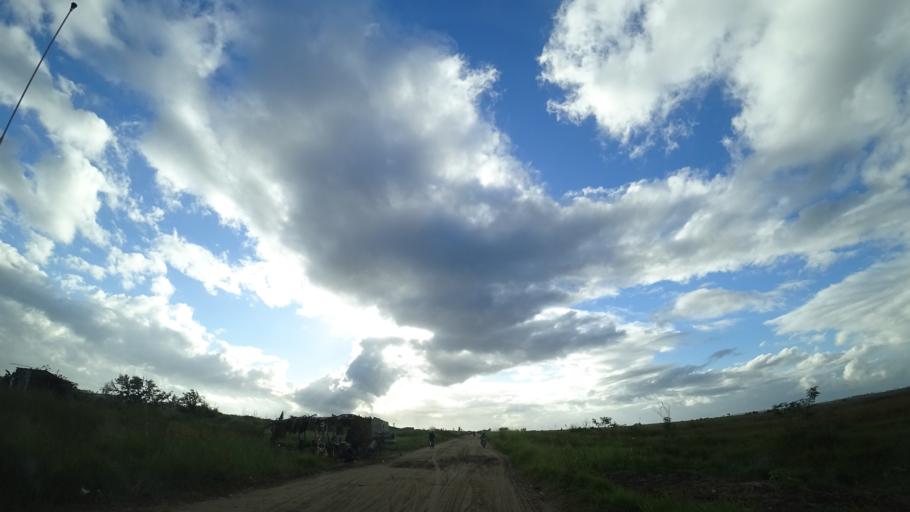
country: MZ
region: Sofala
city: Beira
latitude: -19.7638
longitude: 34.9012
